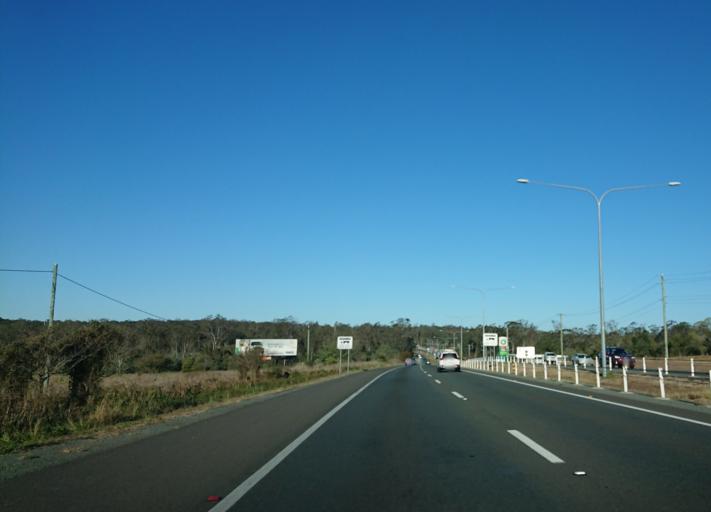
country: AU
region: Queensland
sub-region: Ipswich
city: Brassall
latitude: -27.5777
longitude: 152.7099
